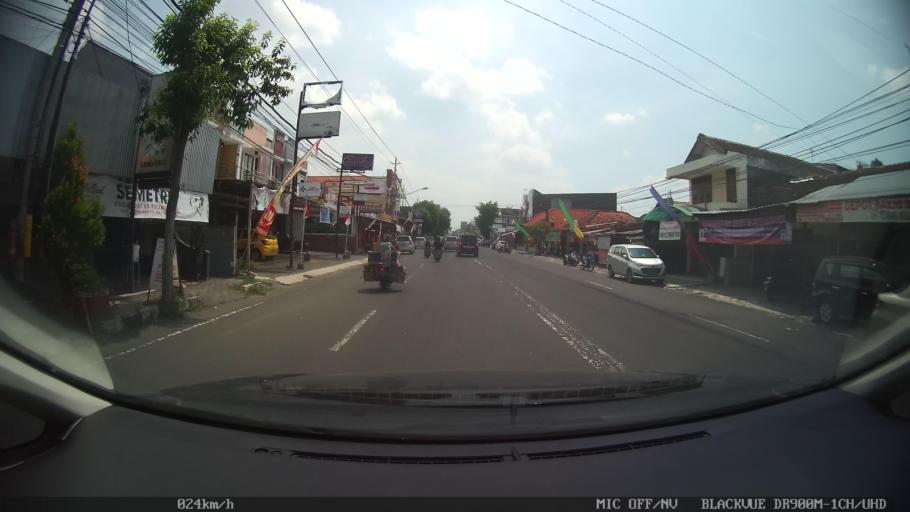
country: ID
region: Daerah Istimewa Yogyakarta
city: Yogyakarta
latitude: -7.8053
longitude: 110.4022
